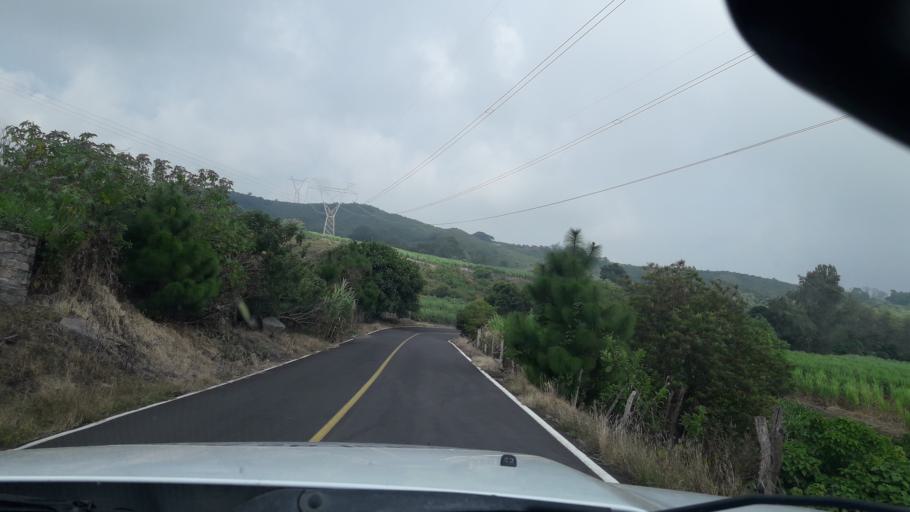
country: MX
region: Colima
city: Queseria
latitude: 19.4091
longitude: -103.6402
